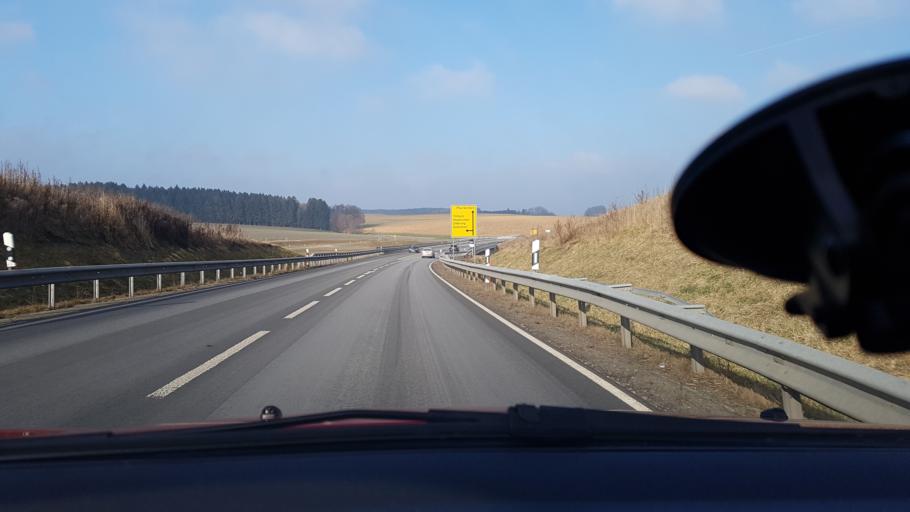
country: DE
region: Bavaria
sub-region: Lower Bavaria
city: Wittibreut
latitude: 48.3703
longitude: 12.9559
